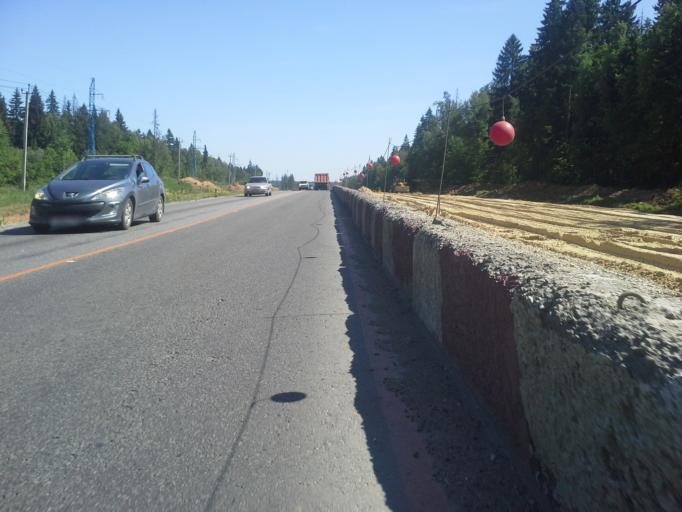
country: RU
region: Moskovskaya
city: Selyatino
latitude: 55.4866
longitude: 37.0445
